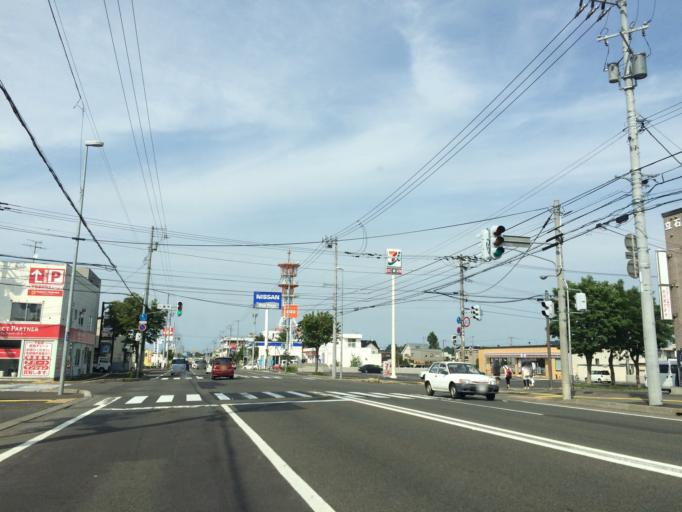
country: JP
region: Hokkaido
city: Ebetsu
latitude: 43.1080
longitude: 141.5448
